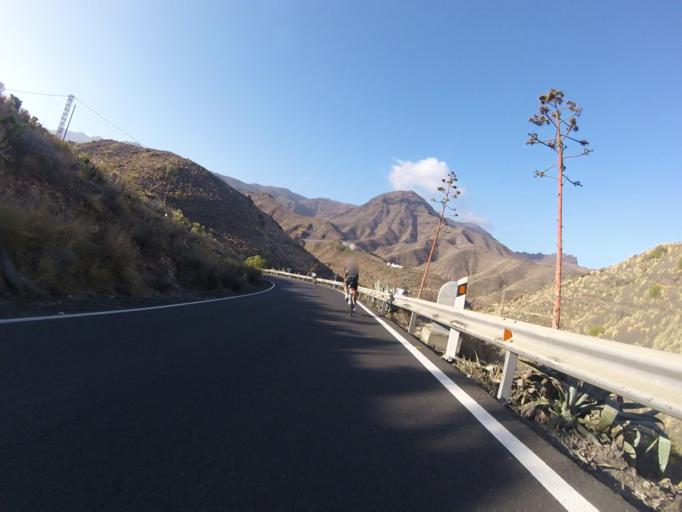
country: ES
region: Canary Islands
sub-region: Provincia de Las Palmas
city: Agaete
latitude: 28.0526
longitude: -15.7315
